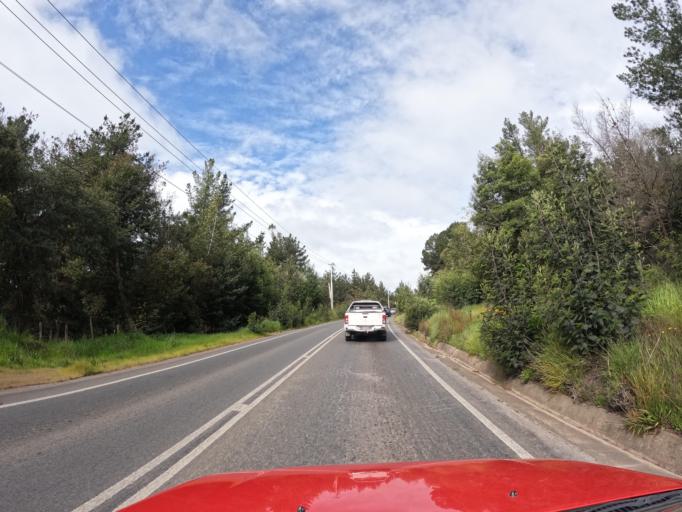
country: CL
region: O'Higgins
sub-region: Provincia de Colchagua
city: Santa Cruz
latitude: -34.3539
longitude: -71.9088
